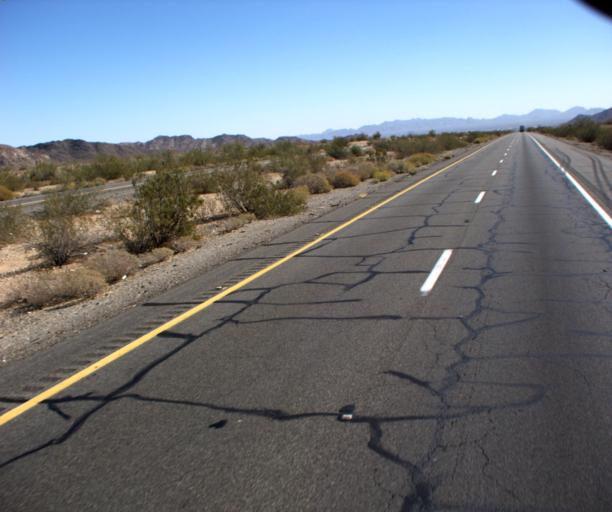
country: US
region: Arizona
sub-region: La Paz County
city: Quartzsite
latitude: 33.6487
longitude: -114.3170
